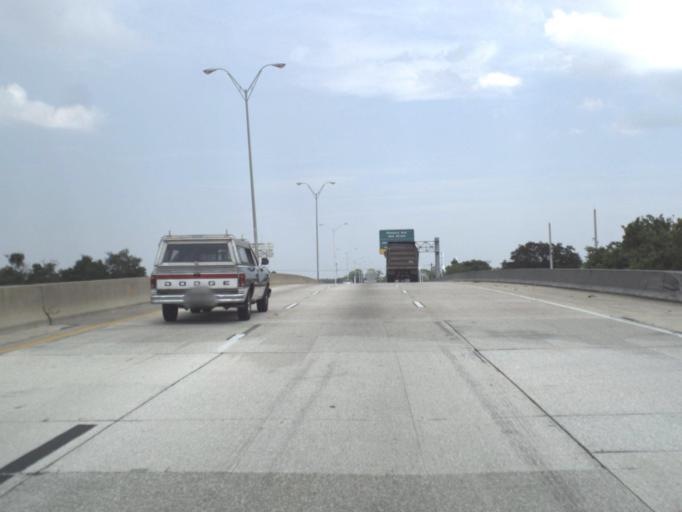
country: US
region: Florida
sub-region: Duval County
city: Jacksonville
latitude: 30.3561
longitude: -81.6465
